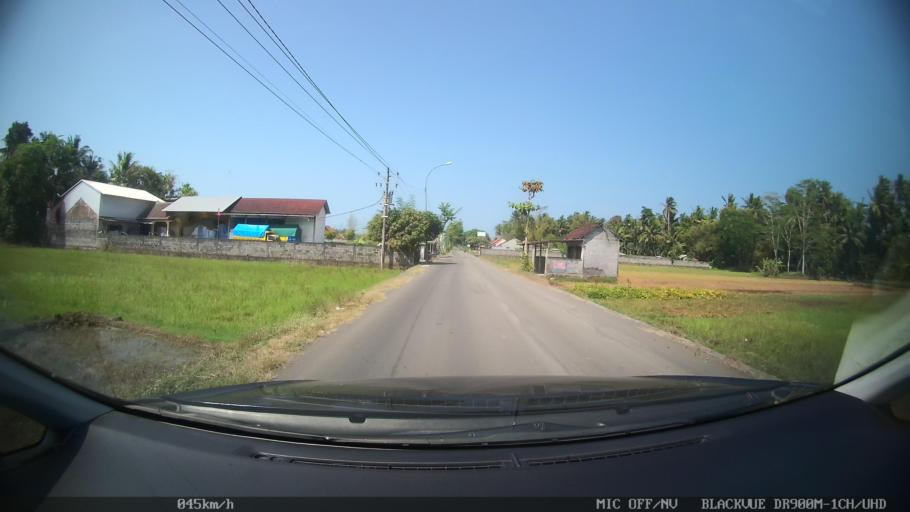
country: ID
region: Daerah Istimewa Yogyakarta
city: Srandakan
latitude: -7.9506
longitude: 110.2192
